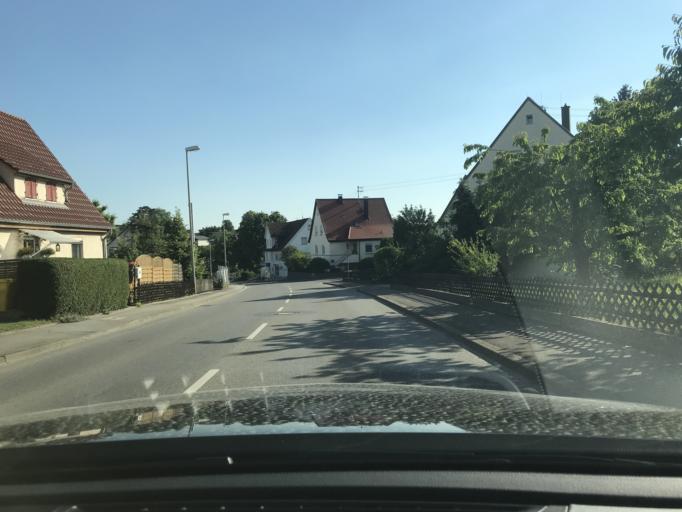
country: DE
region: Baden-Wuerttemberg
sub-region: Regierungsbezirk Stuttgart
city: Schwaikheim
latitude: 48.8681
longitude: 9.3169
